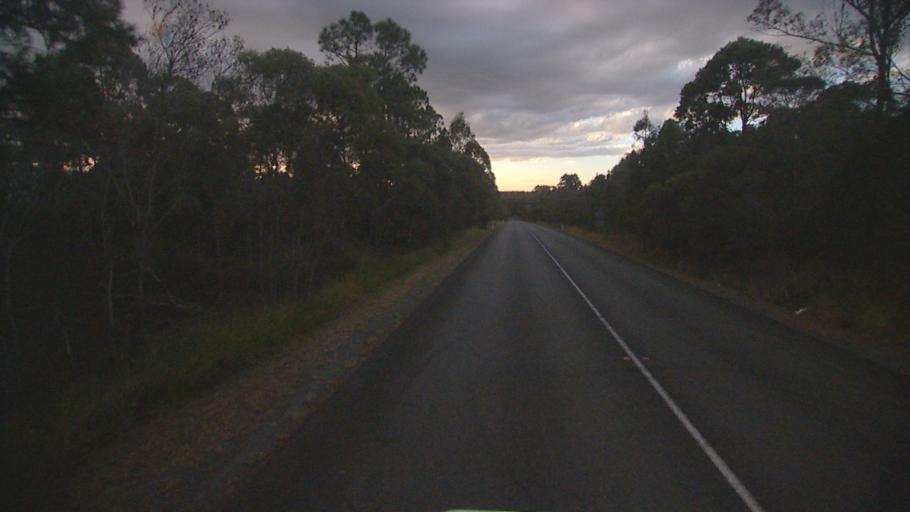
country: AU
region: Queensland
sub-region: Logan
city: Chambers Flat
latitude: -27.7984
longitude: 153.1423
